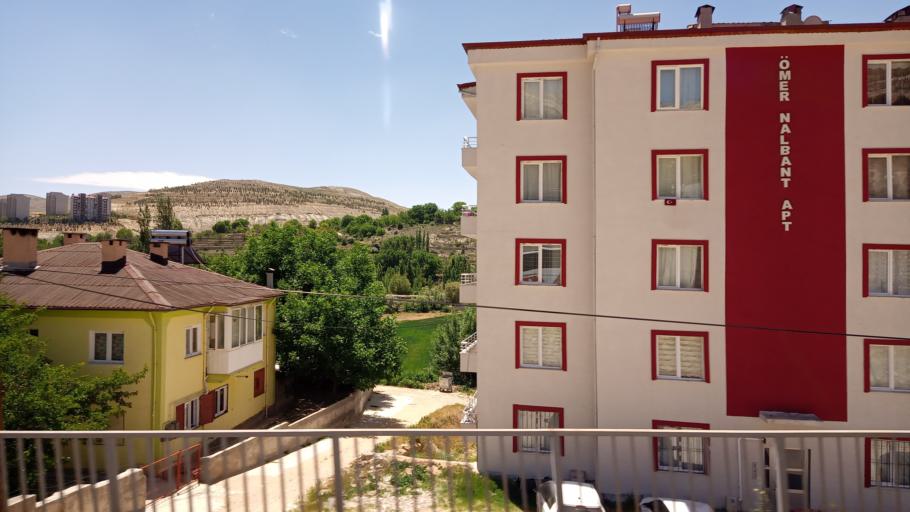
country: TR
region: Sivas
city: Gurun
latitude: 38.7231
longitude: 37.2831
